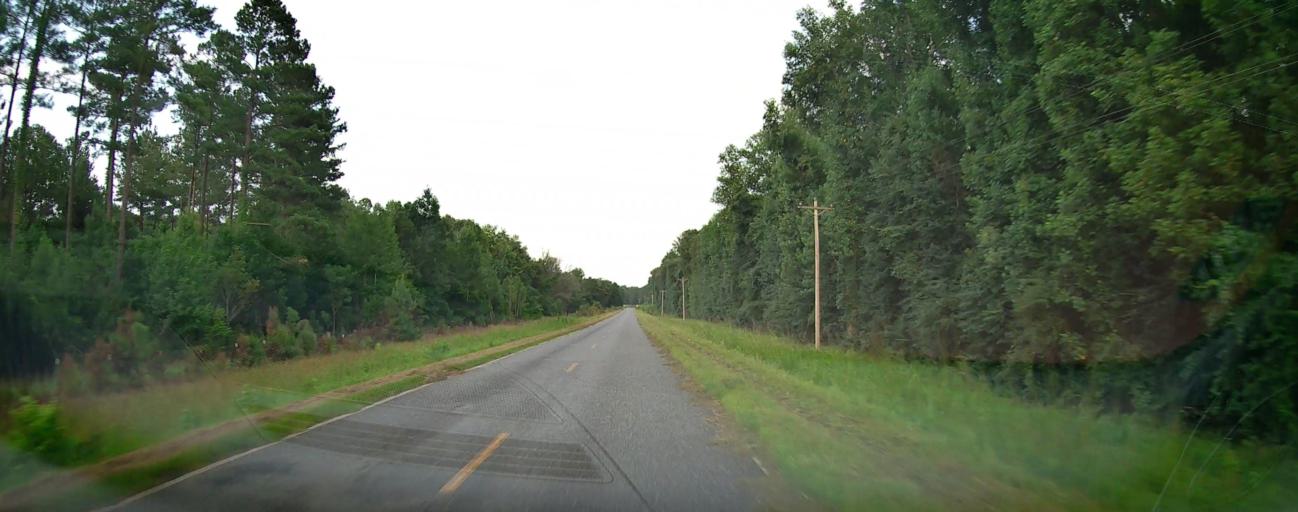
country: US
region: Georgia
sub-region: Crawford County
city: Roberta
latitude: 32.6535
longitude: -84.0387
